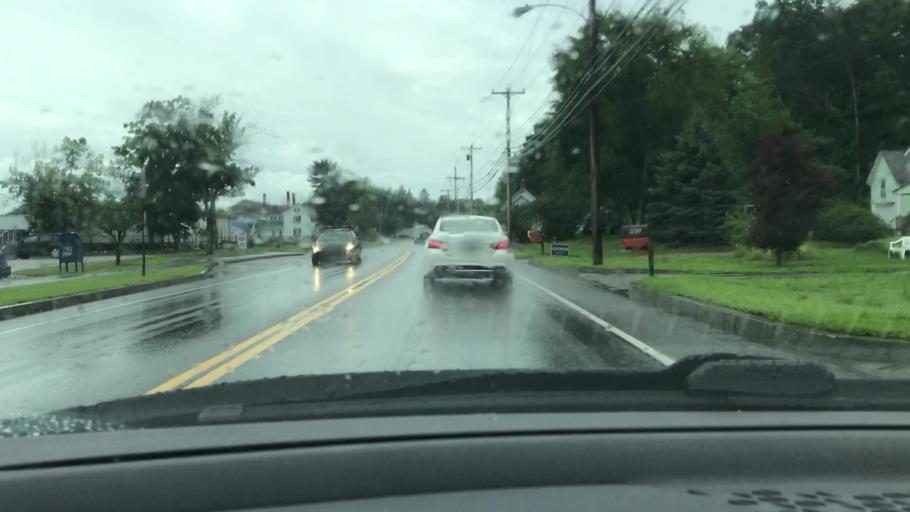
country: US
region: New Hampshire
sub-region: Merrimack County
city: East Concord
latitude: 43.2333
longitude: -71.5618
